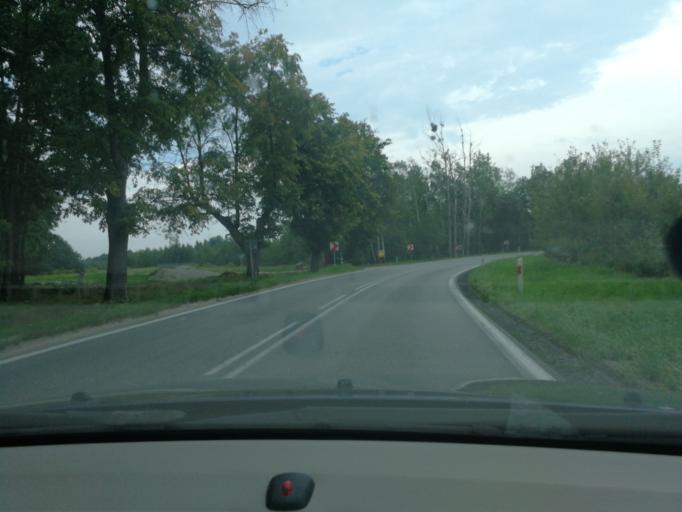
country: PL
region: Masovian Voivodeship
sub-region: Powiat zyrardowski
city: Radziejowice
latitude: 52.0338
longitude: 20.5740
